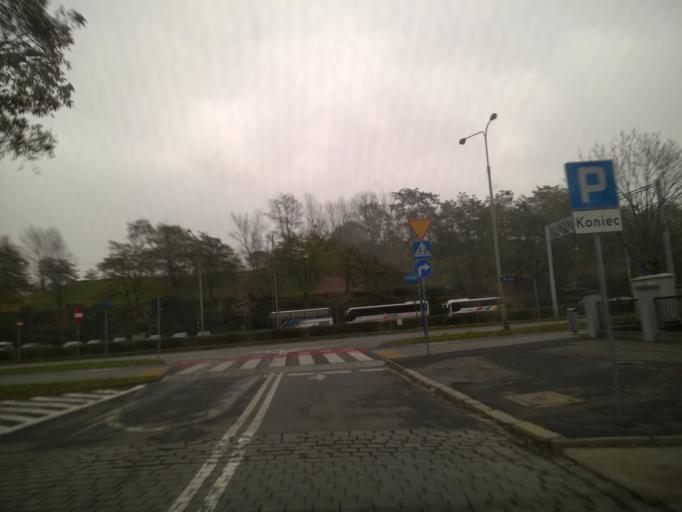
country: PL
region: Lower Silesian Voivodeship
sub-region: Powiat wroclawski
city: Wroclaw
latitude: 51.0909
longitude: 17.0290
